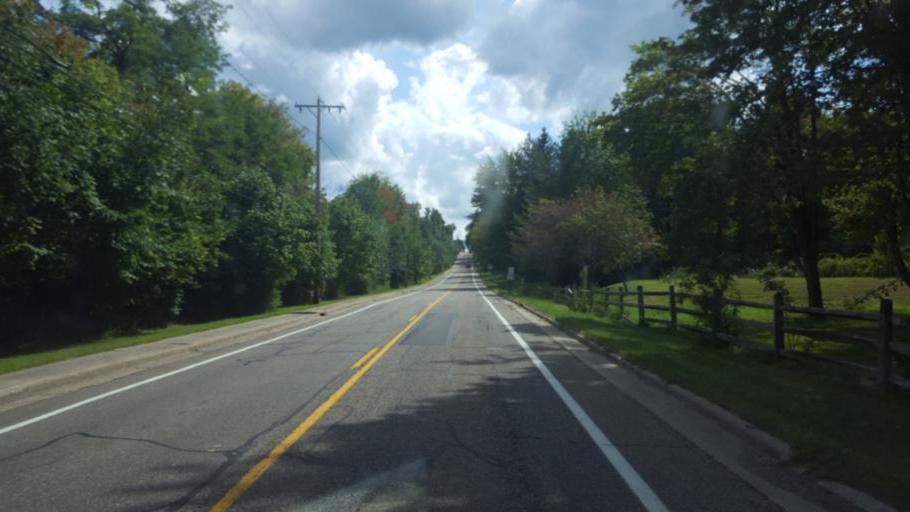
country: US
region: Ohio
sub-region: Portage County
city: Hiram
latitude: 41.3173
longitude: -81.1435
